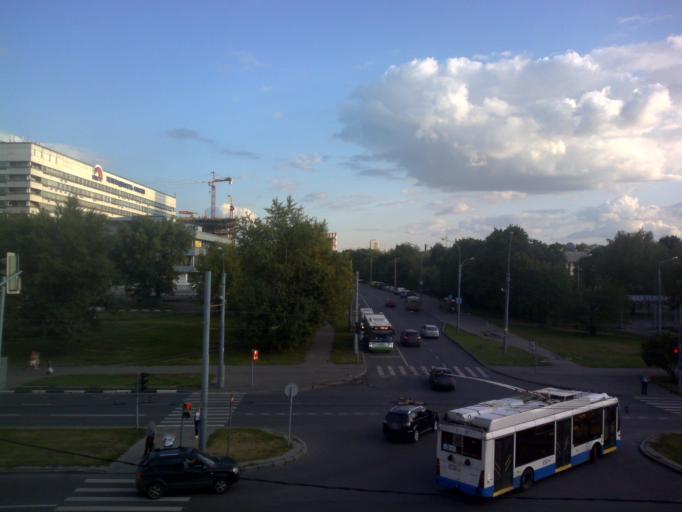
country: RU
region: Moscow
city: Ostankinskiy
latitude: 55.8218
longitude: 37.6169
